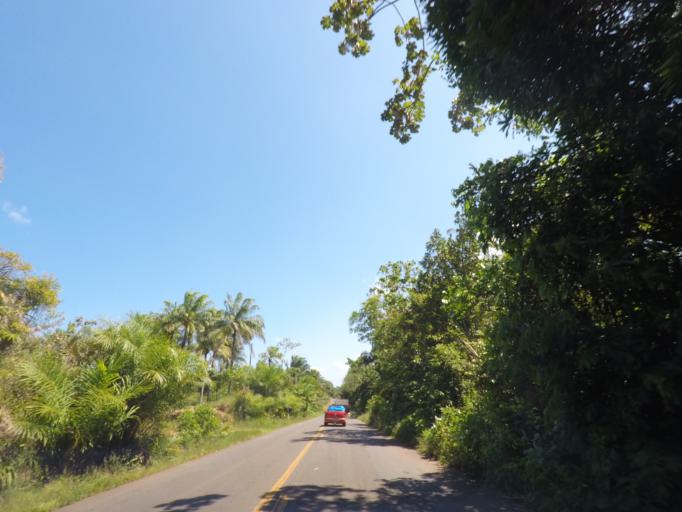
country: BR
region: Bahia
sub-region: Taperoa
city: Taperoa
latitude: -13.4621
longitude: -39.0890
